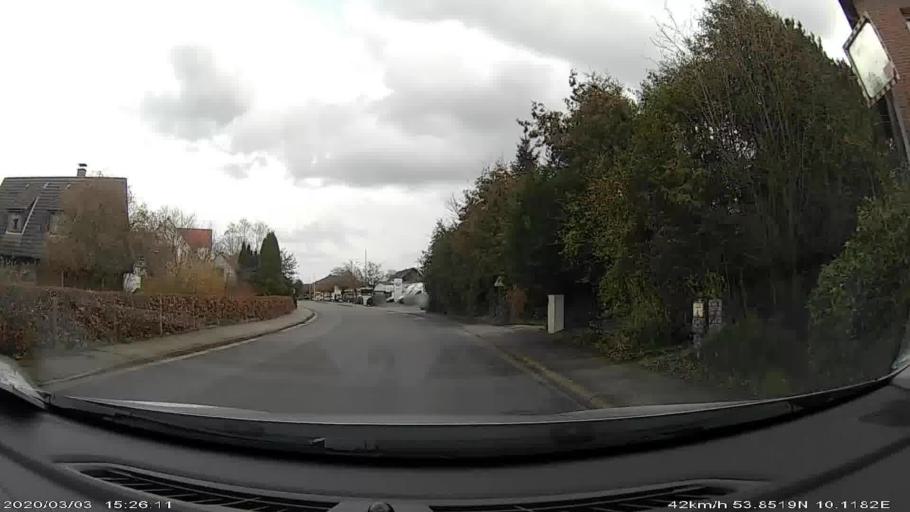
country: DE
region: Schleswig-Holstein
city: Stuvenborn
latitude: 53.8521
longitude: 10.1176
